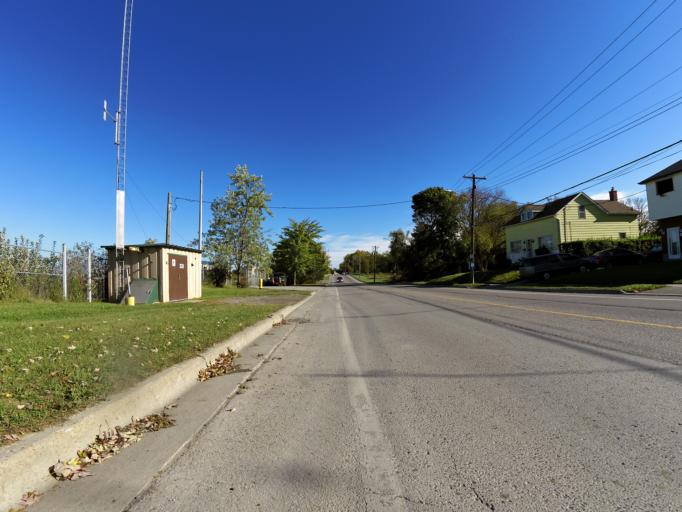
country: CA
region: Ontario
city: Oshawa
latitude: 43.8678
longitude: -78.8330
